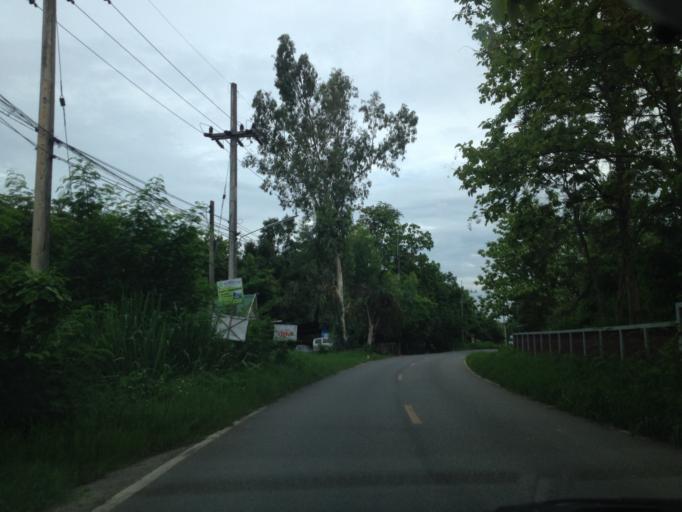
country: TH
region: Chiang Mai
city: Hang Dong
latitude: 18.7405
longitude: 98.9243
